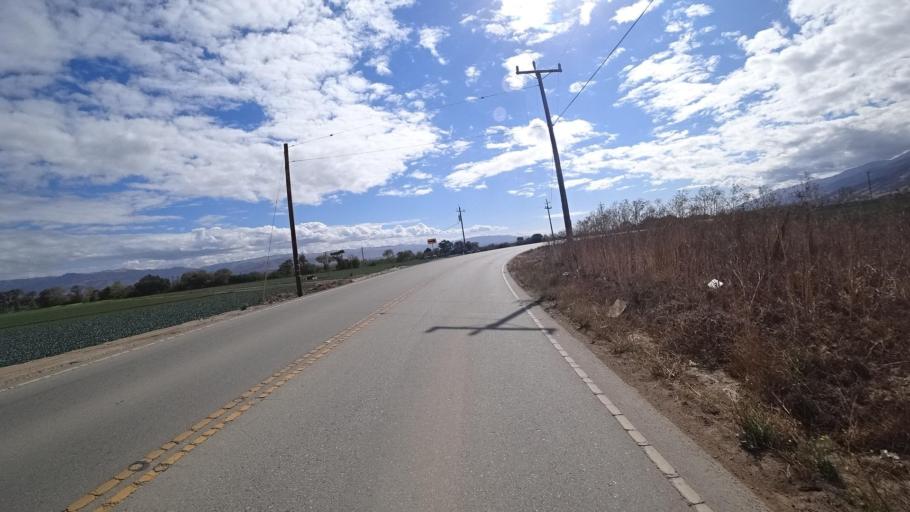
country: US
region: California
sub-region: Monterey County
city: Chualar
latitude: 36.5604
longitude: -121.5549
